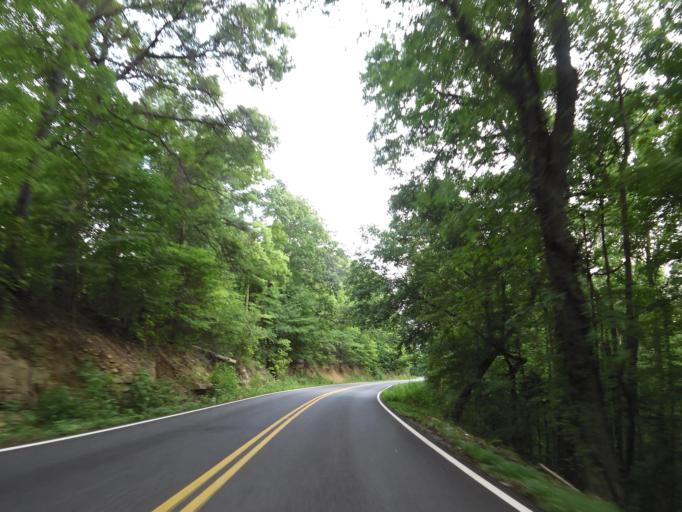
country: US
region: Tennessee
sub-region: Anderson County
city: Clinton
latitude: 36.1415
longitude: -84.2385
